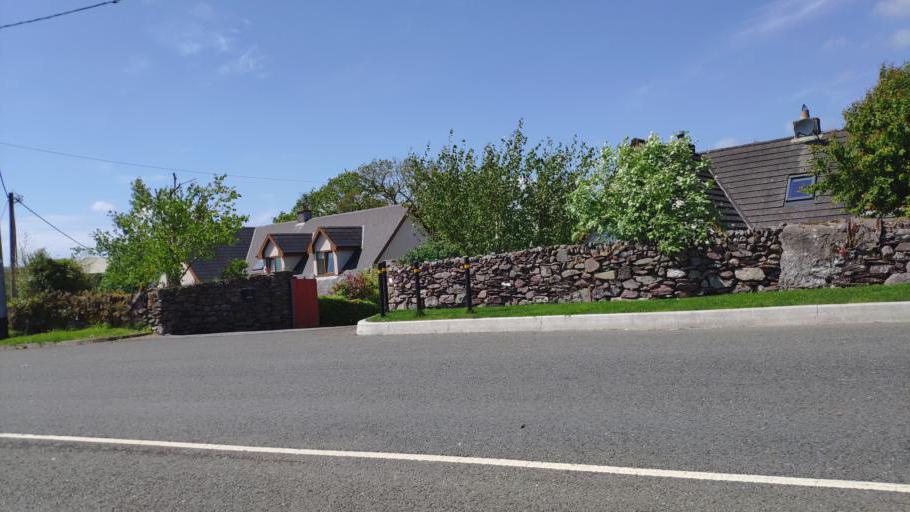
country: IE
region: Munster
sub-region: County Cork
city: Cork
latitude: 51.9258
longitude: -8.4878
